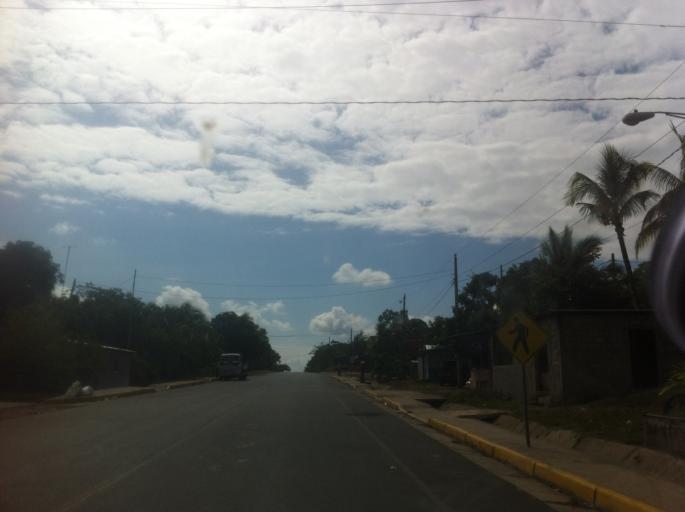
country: NI
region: Rio San Juan
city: San Carlos
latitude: 11.2852
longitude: -84.7203
